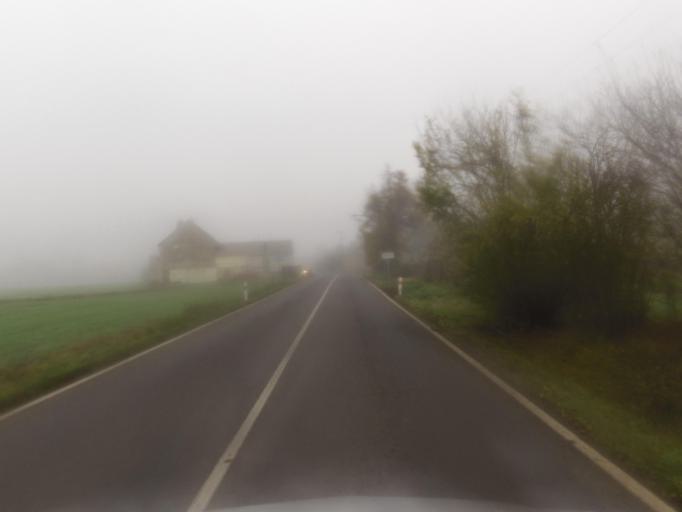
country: CZ
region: Ustecky
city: Peruc
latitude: 50.3952
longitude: 13.9754
